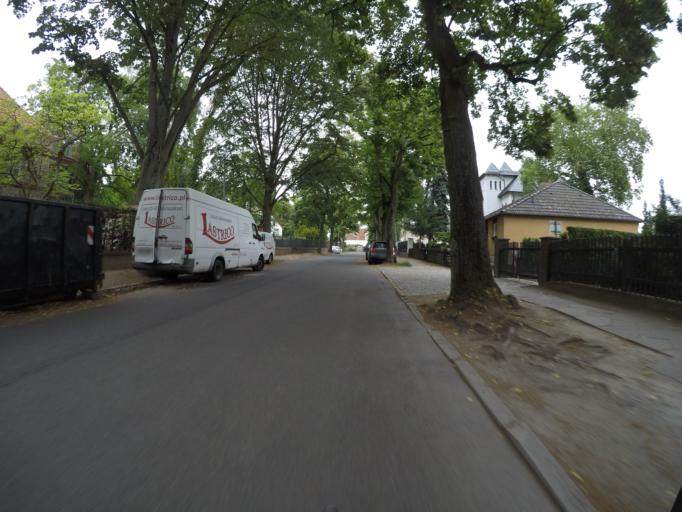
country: DE
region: Berlin
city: Tegel
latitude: 52.5921
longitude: 13.2748
